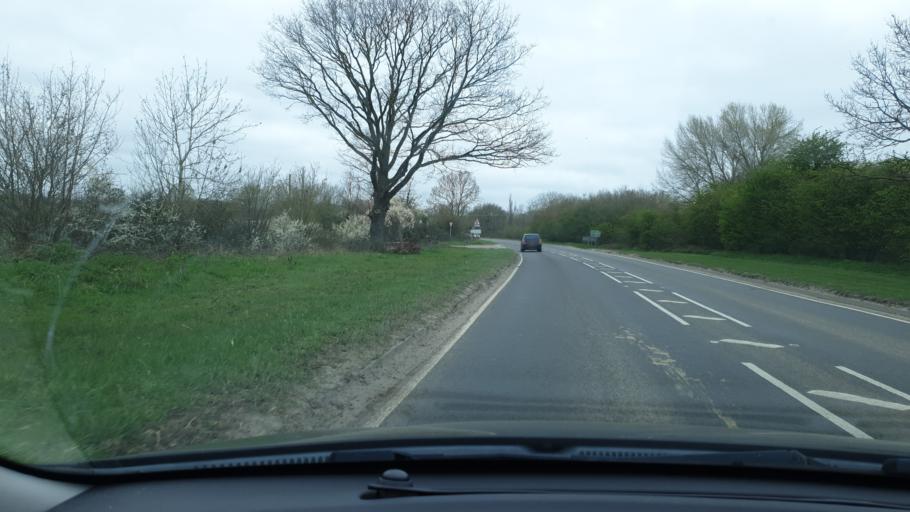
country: GB
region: England
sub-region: Essex
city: Great Horkesley
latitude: 51.9664
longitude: 0.8682
